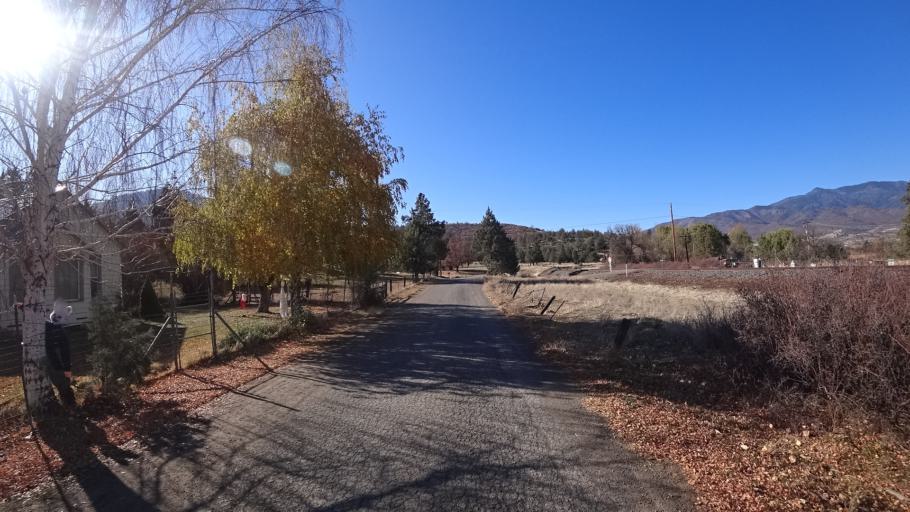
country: US
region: California
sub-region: Siskiyou County
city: Montague
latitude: 41.8956
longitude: -122.5187
